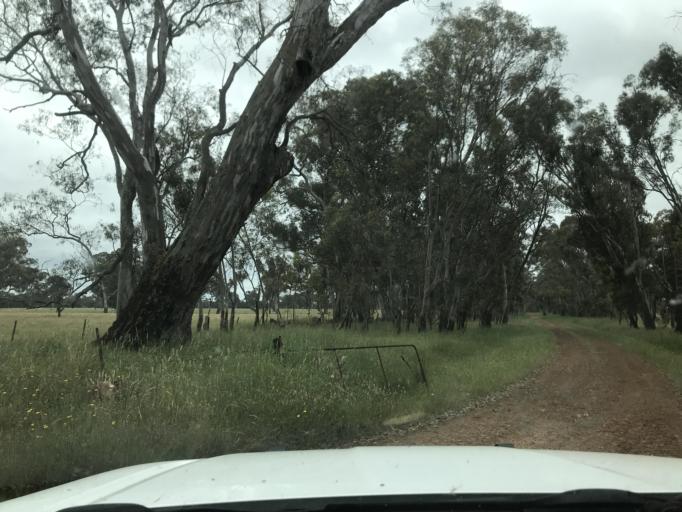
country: AU
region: South Australia
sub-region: Wattle Range
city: Penola
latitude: -37.2442
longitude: 141.1221
